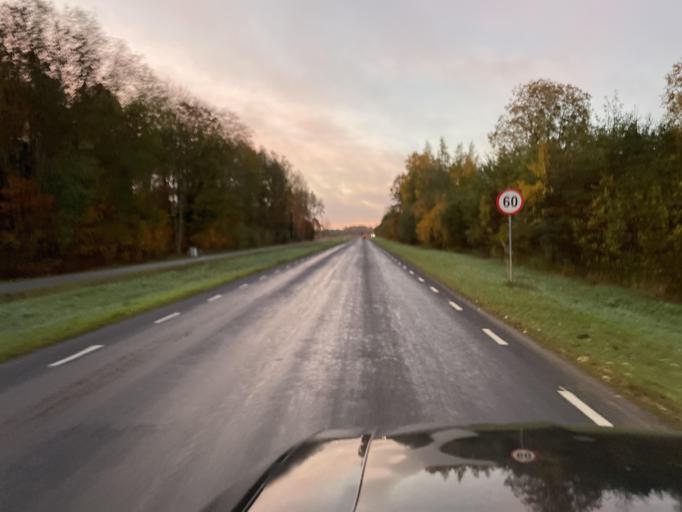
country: EE
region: Harju
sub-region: Nissi vald
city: Riisipere
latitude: 59.2428
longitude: 24.2434
